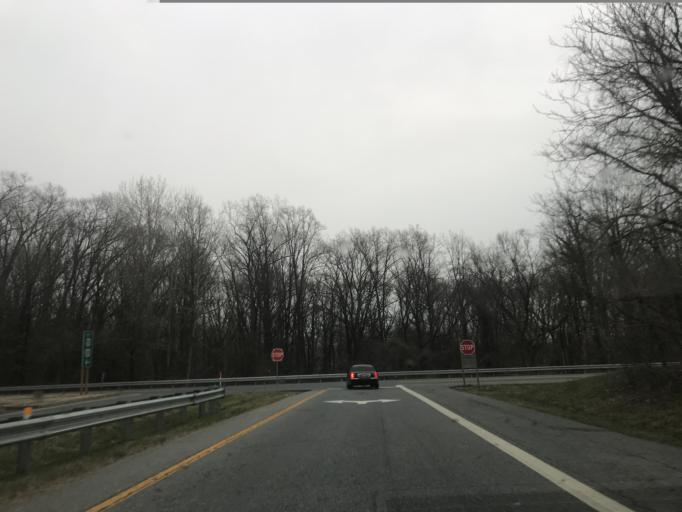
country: US
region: Maryland
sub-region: Anne Arundel County
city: Arnold
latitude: 39.0221
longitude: -76.4717
